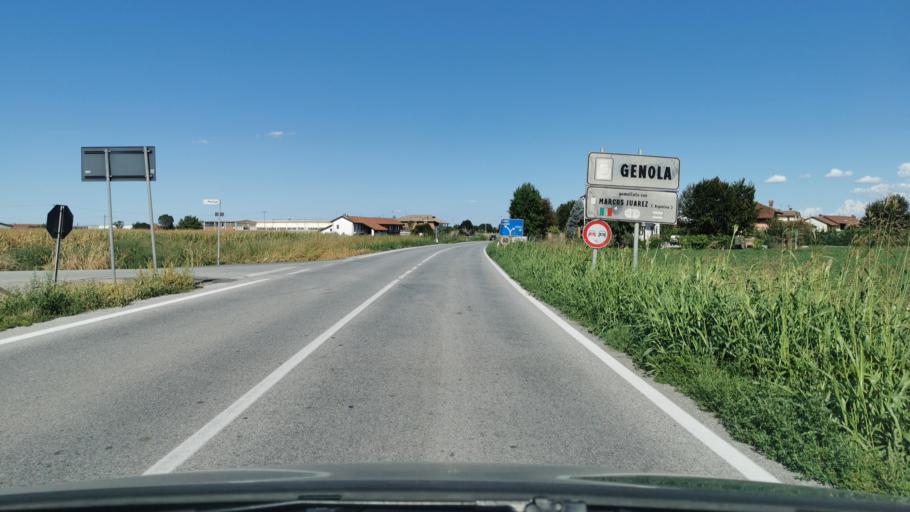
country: IT
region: Piedmont
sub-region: Provincia di Cuneo
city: Genola
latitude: 44.5870
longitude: 7.6508
